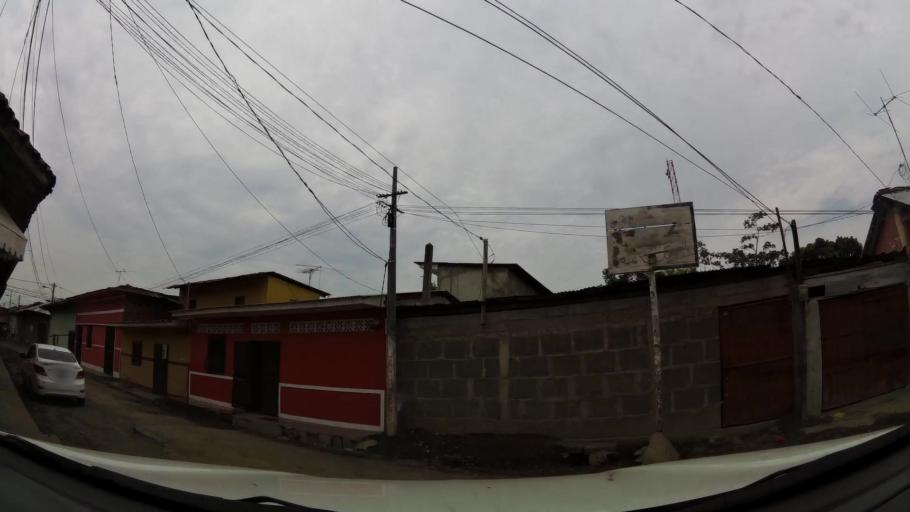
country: NI
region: Granada
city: Granada
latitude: 11.9286
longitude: -85.9515
